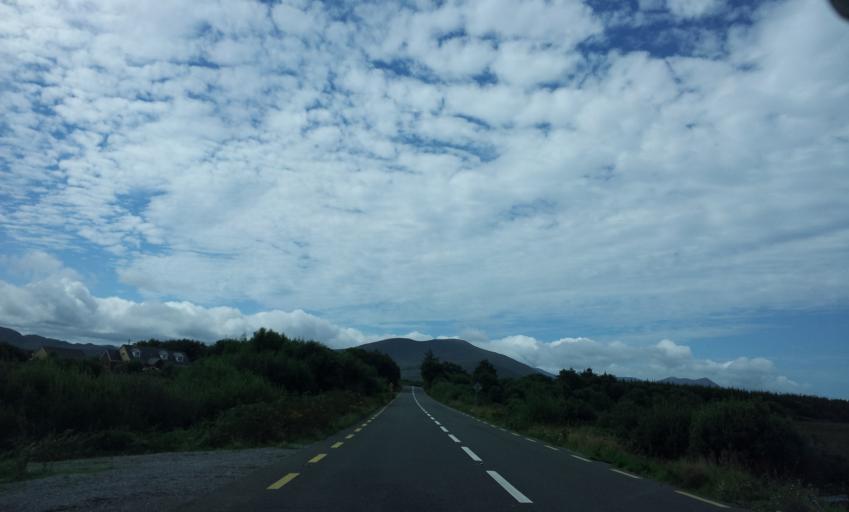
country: IE
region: Munster
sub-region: Ciarrai
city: Killorglin
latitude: 52.0909
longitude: -9.8475
